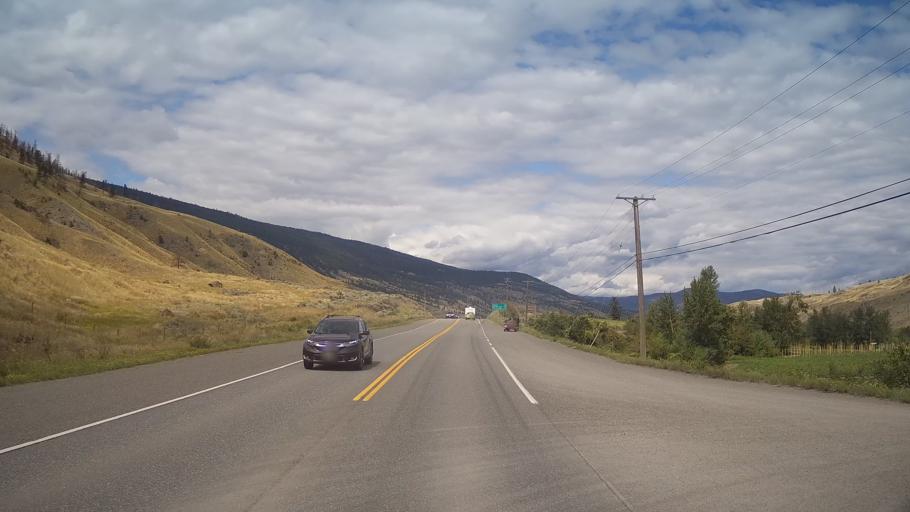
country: CA
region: British Columbia
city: Cache Creek
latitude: 50.8266
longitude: -121.3534
